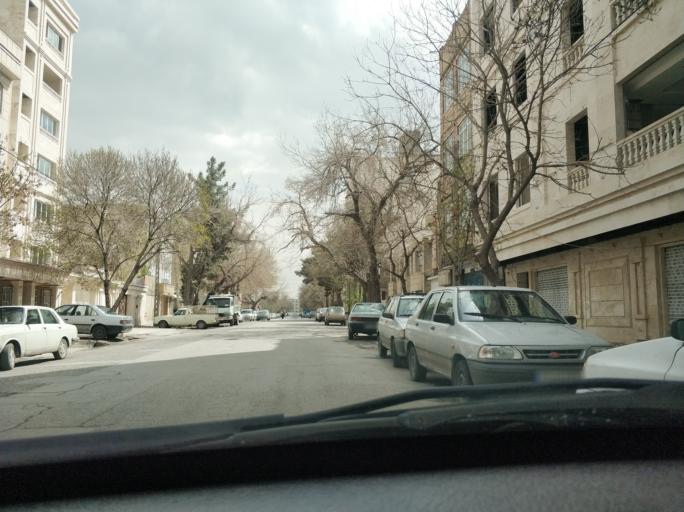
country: IR
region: Razavi Khorasan
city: Mashhad
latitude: 36.2763
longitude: 59.5717
